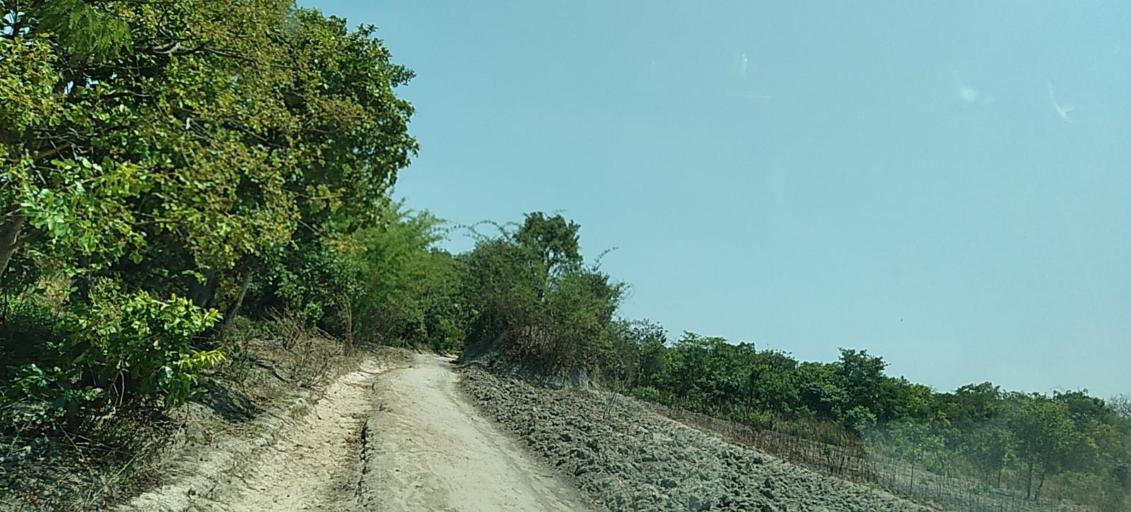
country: ZM
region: Copperbelt
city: Luanshya
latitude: -12.9844
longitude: 28.3292
